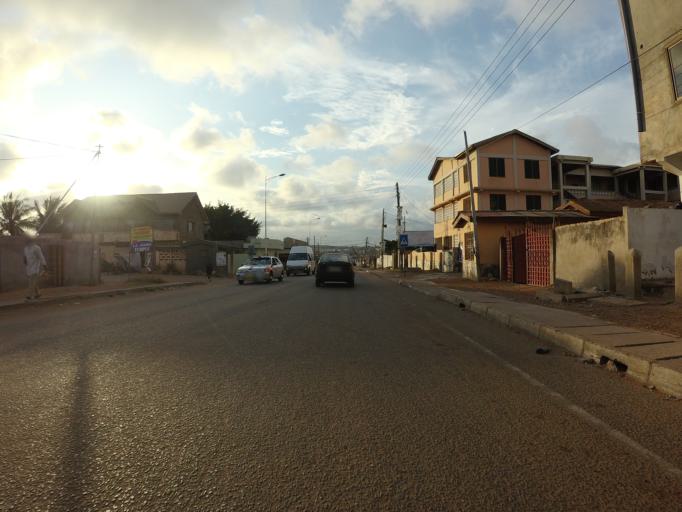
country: GH
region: Greater Accra
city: Teshi Old Town
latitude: 5.5945
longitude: -0.1284
